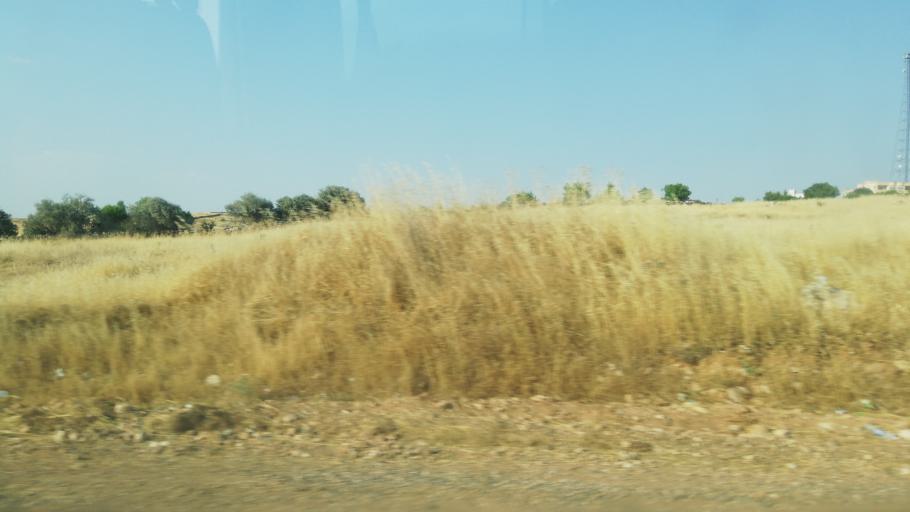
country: TR
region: Mardin
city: Acirli
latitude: 37.4426
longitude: 41.2886
